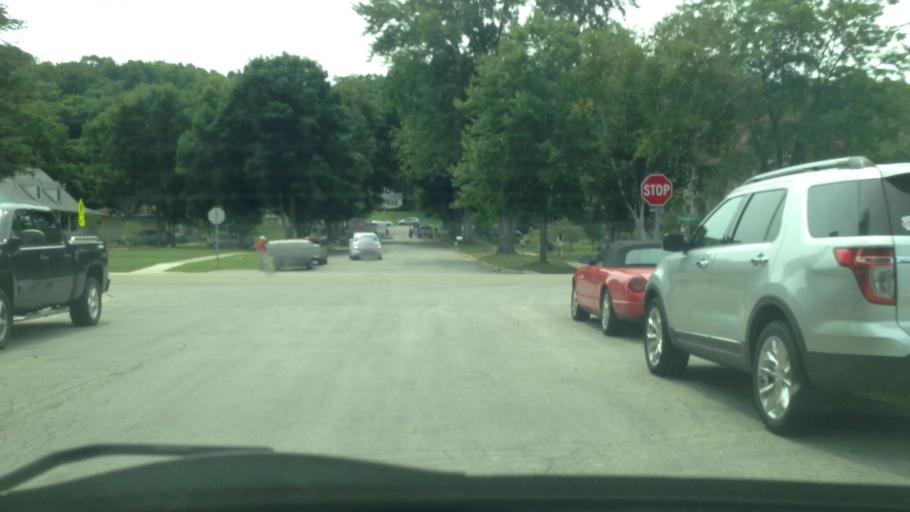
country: US
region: Minnesota
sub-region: Fillmore County
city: Preston
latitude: 43.7143
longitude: -91.9741
